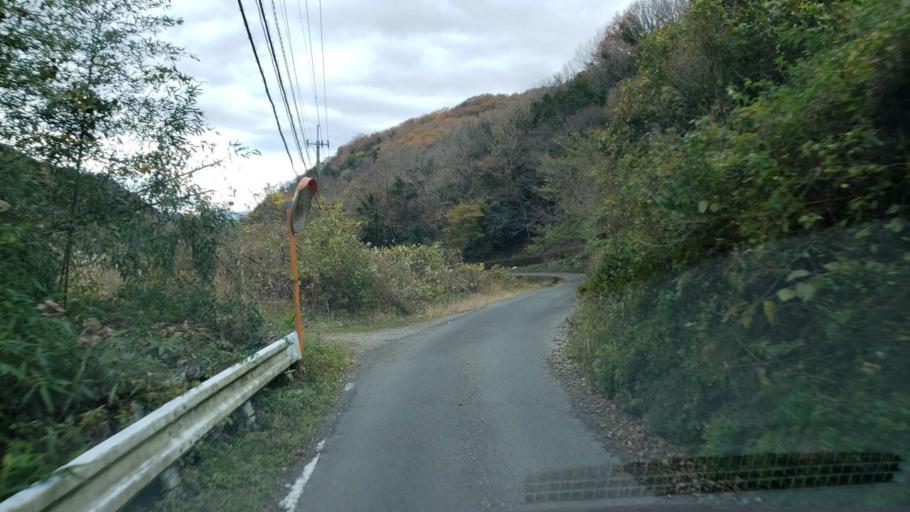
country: JP
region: Tokushima
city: Wakimachi
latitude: 34.1213
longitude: 134.2258
